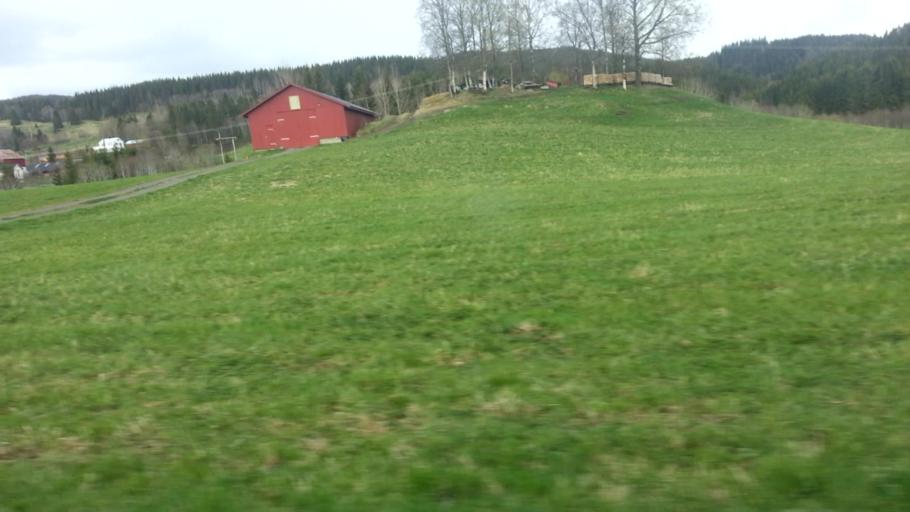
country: NO
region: Nord-Trondelag
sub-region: Levanger
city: Skogn
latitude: 63.6572
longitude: 11.2365
